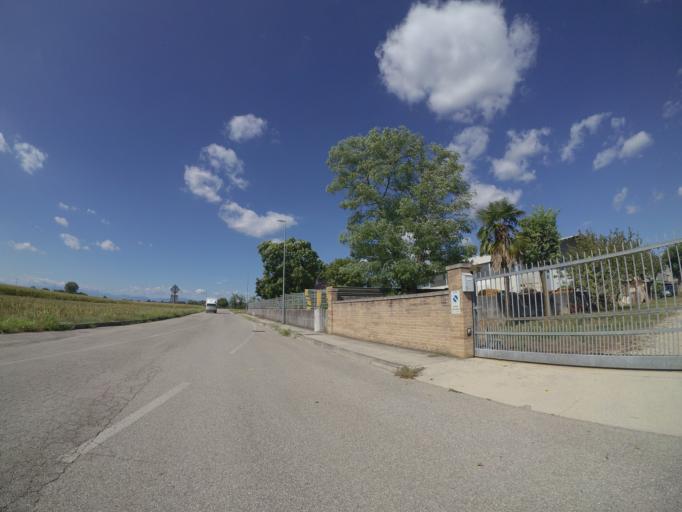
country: IT
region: Friuli Venezia Giulia
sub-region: Provincia di Udine
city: Talmassons
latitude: 45.9308
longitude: 13.1441
